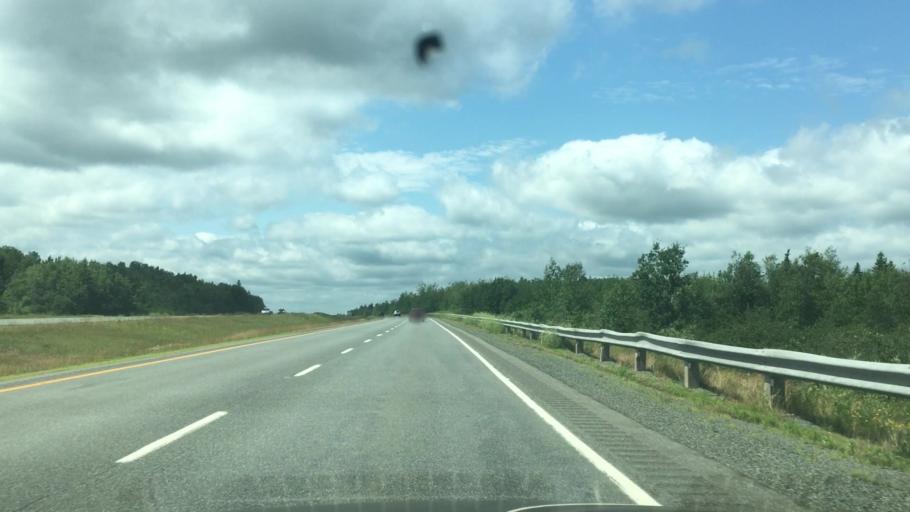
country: CA
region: Nova Scotia
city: Oxford
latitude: 45.7129
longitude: -63.9436
